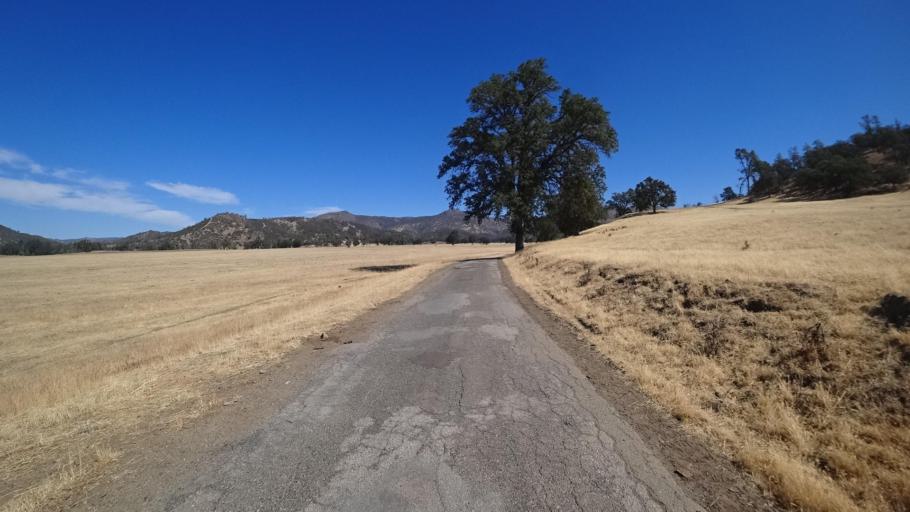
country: US
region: California
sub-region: Fresno County
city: Coalinga
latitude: 36.2059
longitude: -120.7021
